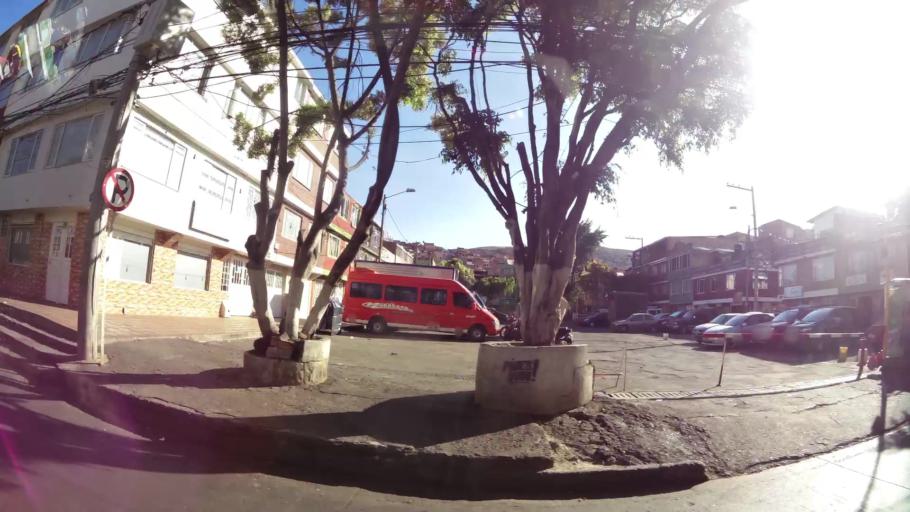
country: CO
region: Cundinamarca
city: Soacha
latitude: 4.5699
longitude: -74.1511
